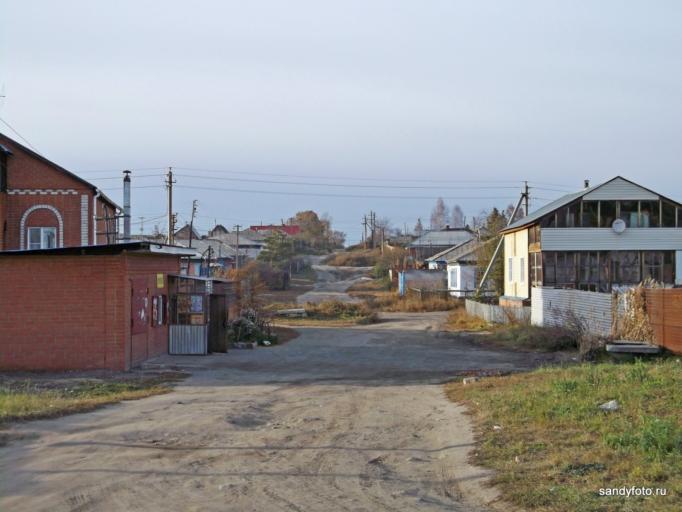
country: RU
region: Chelyabinsk
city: Troitsk
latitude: 54.0729
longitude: 61.5875
